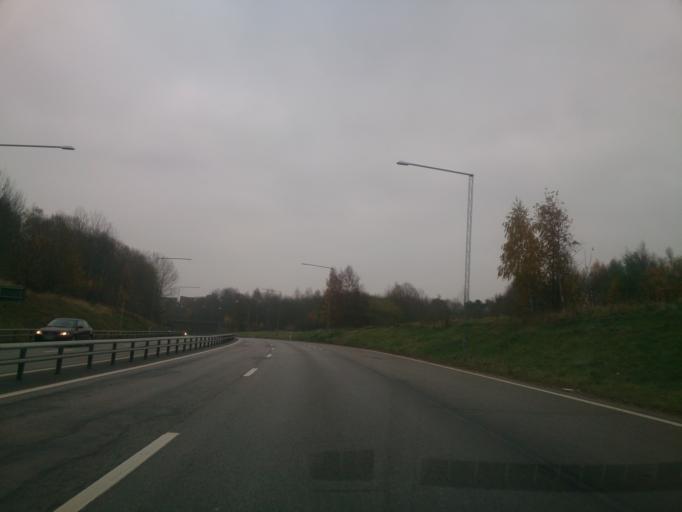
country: SE
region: OEstergoetland
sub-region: Norrkopings Kommun
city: Norrkoping
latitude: 58.5758
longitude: 16.1635
